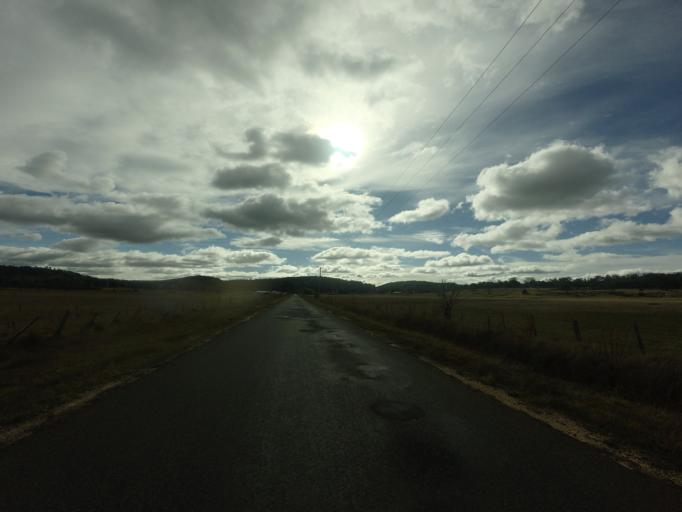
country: AU
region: Tasmania
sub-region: Brighton
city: Bridgewater
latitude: -42.4061
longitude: 147.3948
